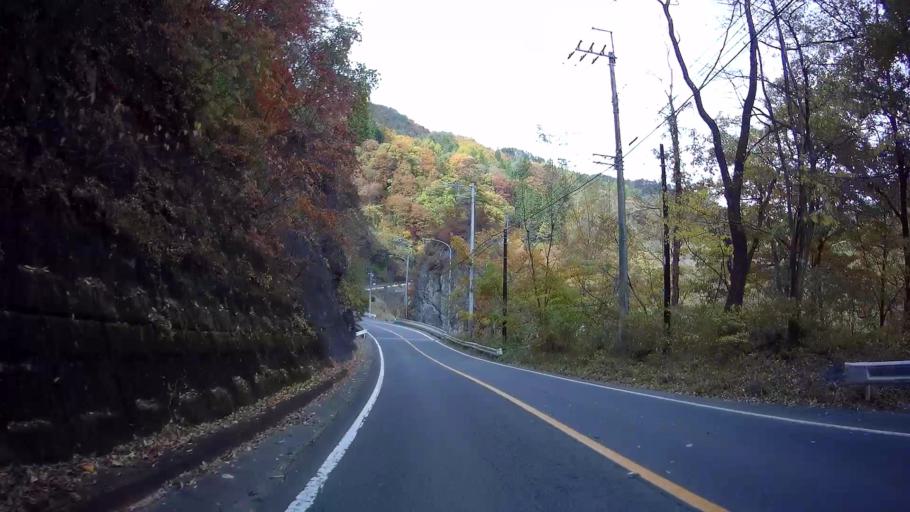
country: JP
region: Gunma
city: Nakanojomachi
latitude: 36.6014
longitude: 138.6306
